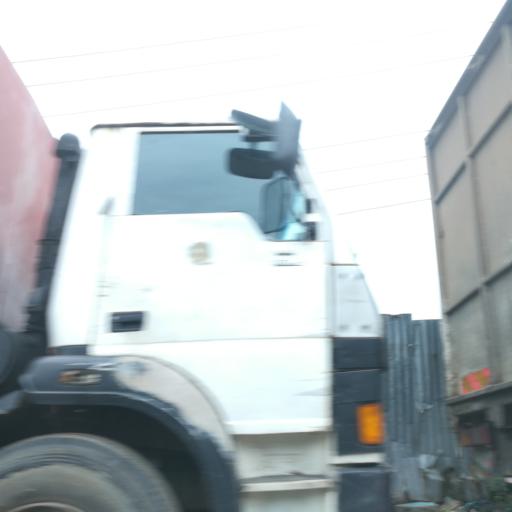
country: NG
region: Lagos
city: Makoko
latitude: 6.5008
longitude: 3.3804
